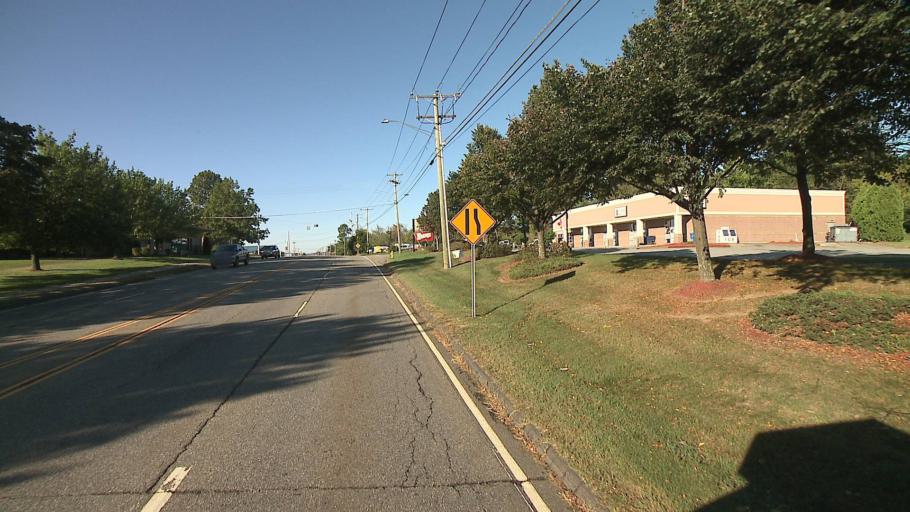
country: US
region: Connecticut
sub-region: Litchfield County
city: Torrington
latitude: 41.8205
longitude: -73.0852
